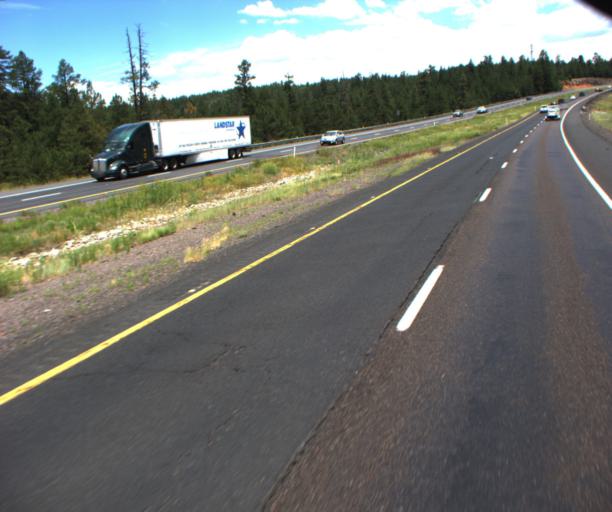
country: US
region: Arizona
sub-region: Coconino County
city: Mountainaire
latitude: 35.0407
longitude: -111.6851
